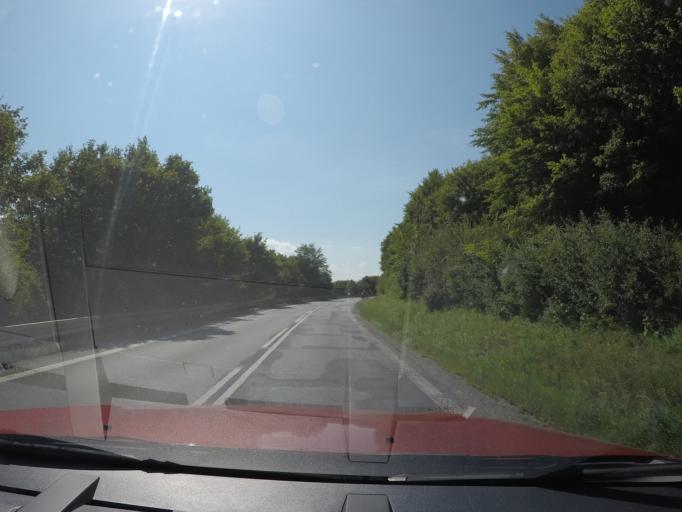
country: SK
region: Presovsky
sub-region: Okres Presov
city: Presov
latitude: 48.9451
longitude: 21.2396
